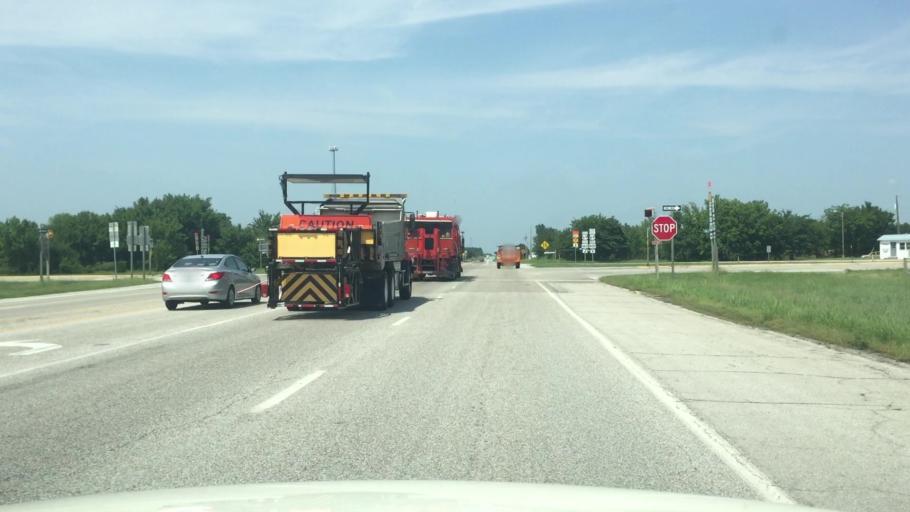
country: US
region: Kansas
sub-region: Cherokee County
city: Galena
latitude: 37.1774
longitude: -94.7043
